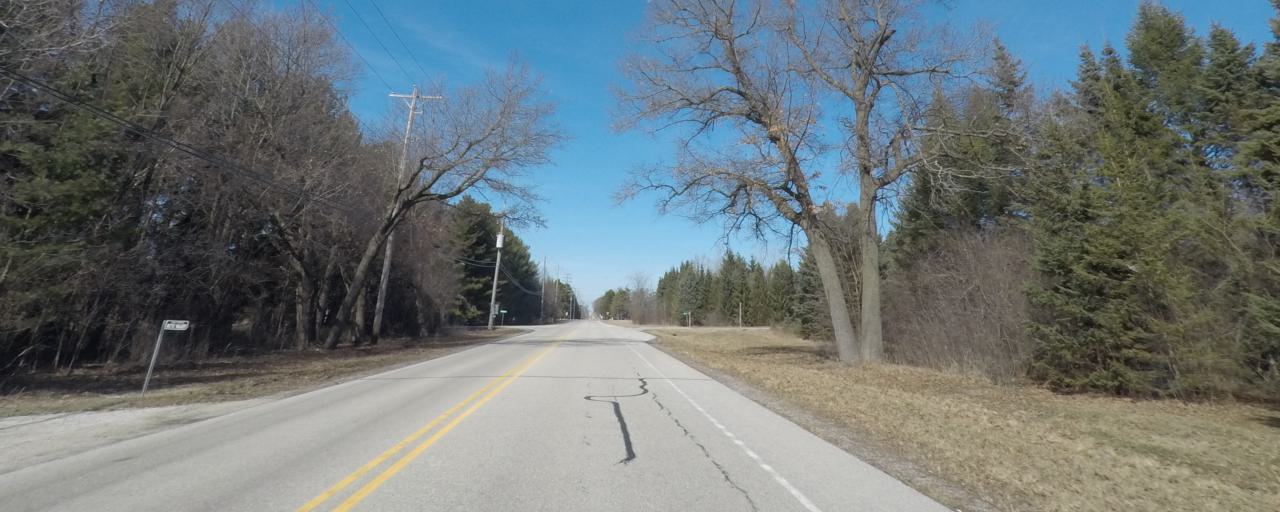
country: US
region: Wisconsin
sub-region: Waukesha County
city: Merton
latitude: 43.1392
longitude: -88.3271
